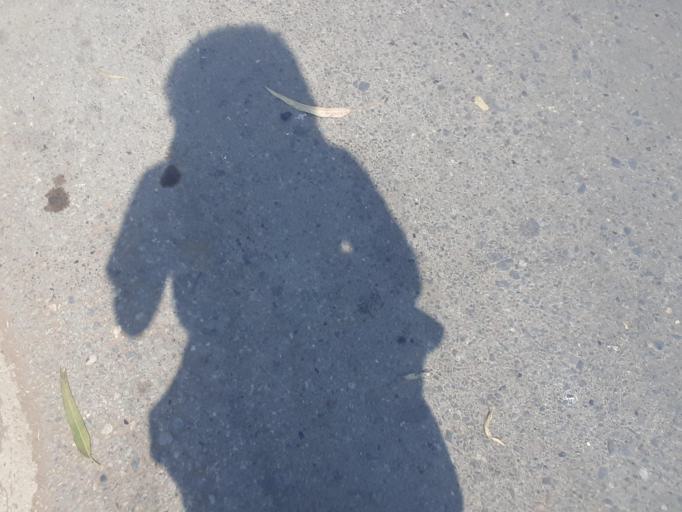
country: ZM
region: Lusaka
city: Lusaka
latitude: -15.3543
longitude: 28.2799
